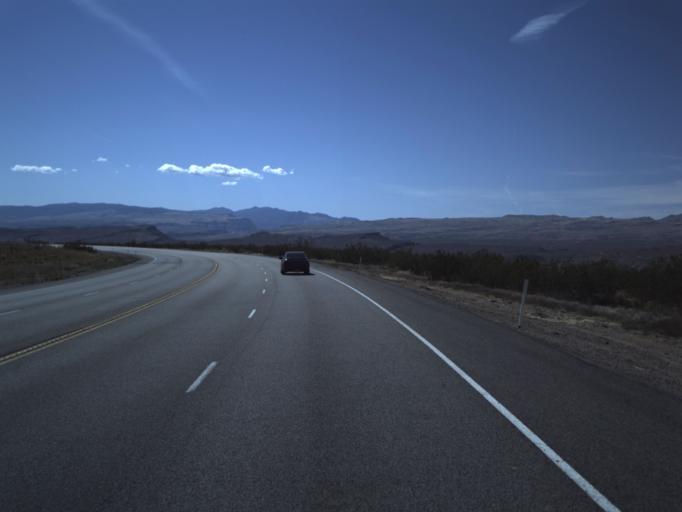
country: US
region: Utah
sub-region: Washington County
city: Santa Clara
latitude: 37.1530
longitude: -113.6064
